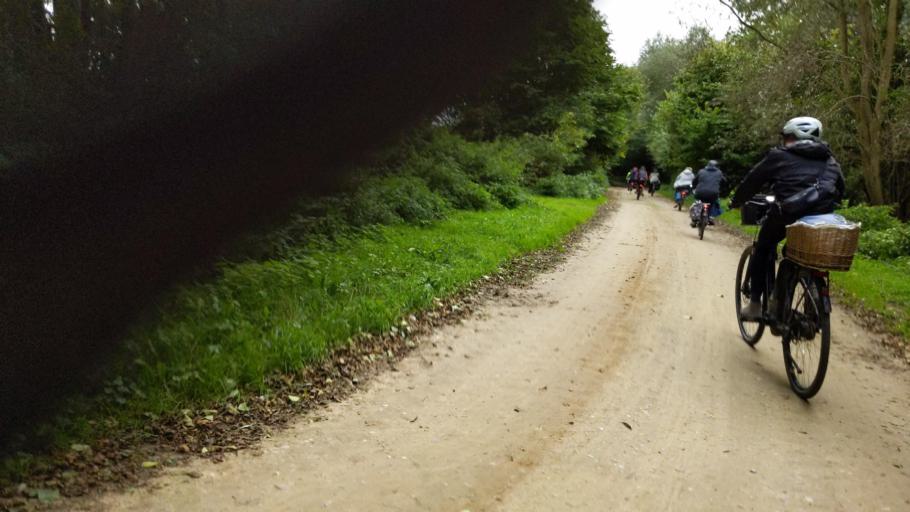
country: DE
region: Schleswig-Holstein
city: Buchholz
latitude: 53.7474
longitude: 10.7589
